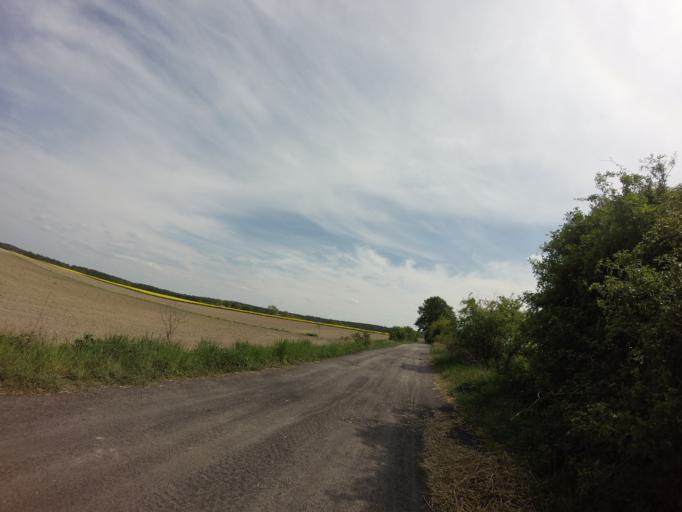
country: PL
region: West Pomeranian Voivodeship
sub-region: Powiat choszczenski
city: Choszczno
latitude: 53.2057
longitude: 15.4034
